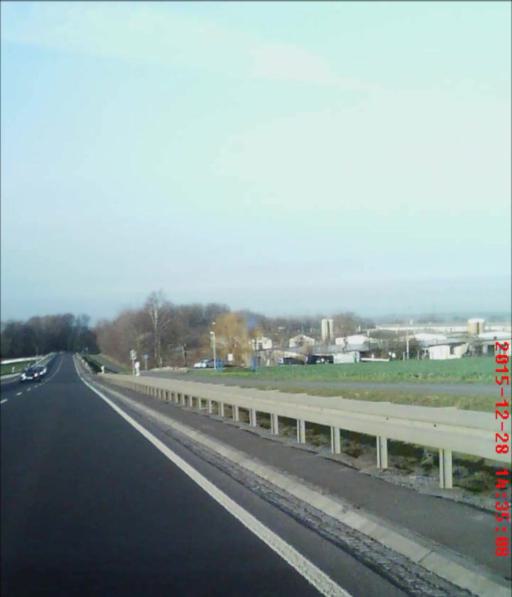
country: DE
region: Thuringia
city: Grossobringen
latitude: 51.0375
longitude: 11.3373
